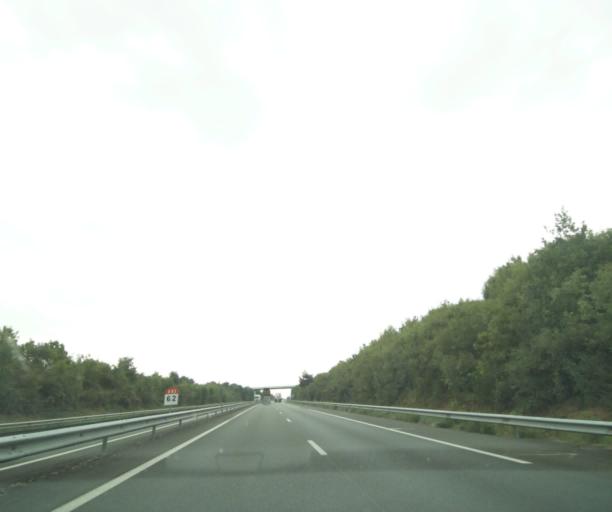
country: FR
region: Pays de la Loire
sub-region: Departement de la Vendee
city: Bournezeau
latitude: 46.6550
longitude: -1.1541
